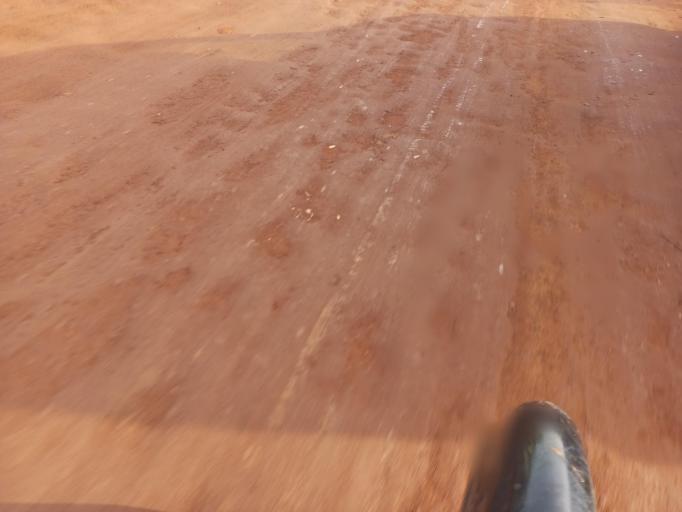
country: ML
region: Bamako
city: Bamako
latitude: 12.5254
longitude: -7.9948
